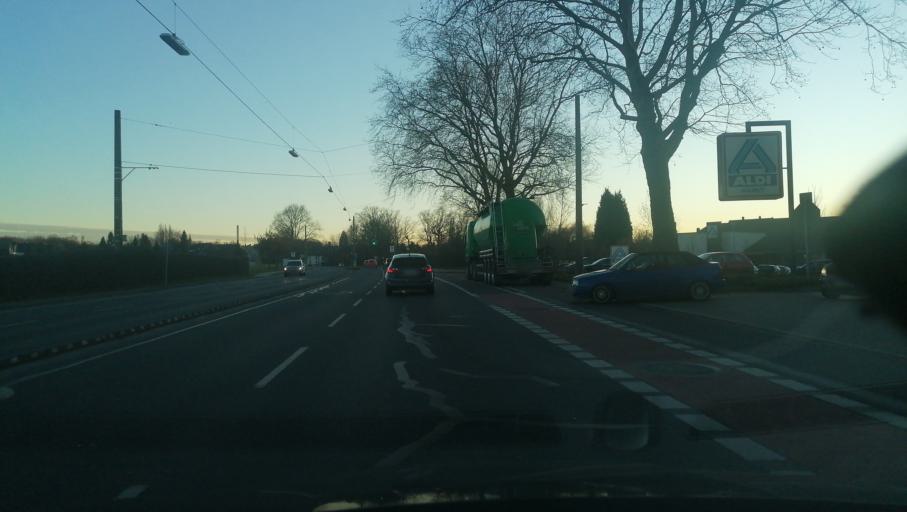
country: DE
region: North Rhine-Westphalia
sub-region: Regierungsbezirk Munster
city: Recklinghausen
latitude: 51.5922
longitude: 7.1813
